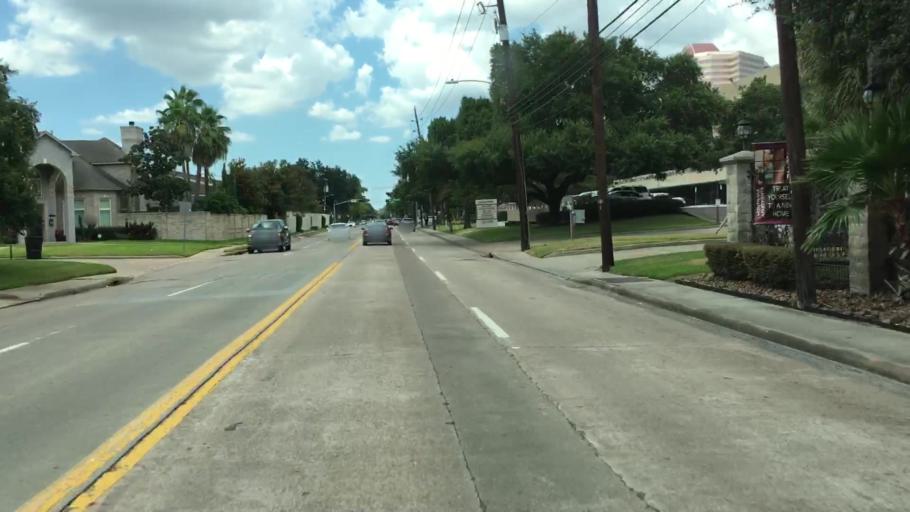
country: US
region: Texas
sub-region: Harris County
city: Hunters Creek Village
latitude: 29.7444
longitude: -95.4670
